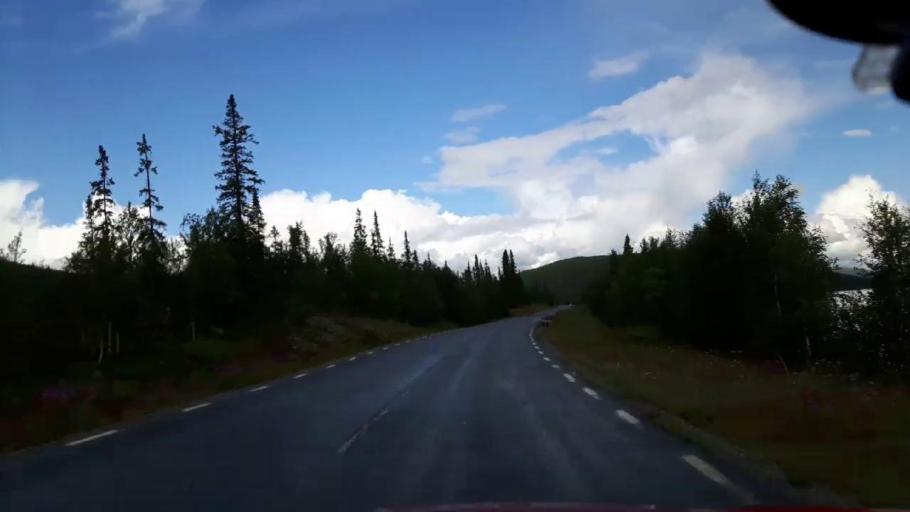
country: SE
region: Vaesterbotten
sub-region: Vilhelmina Kommun
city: Sjoberg
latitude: 65.0120
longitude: 15.1738
